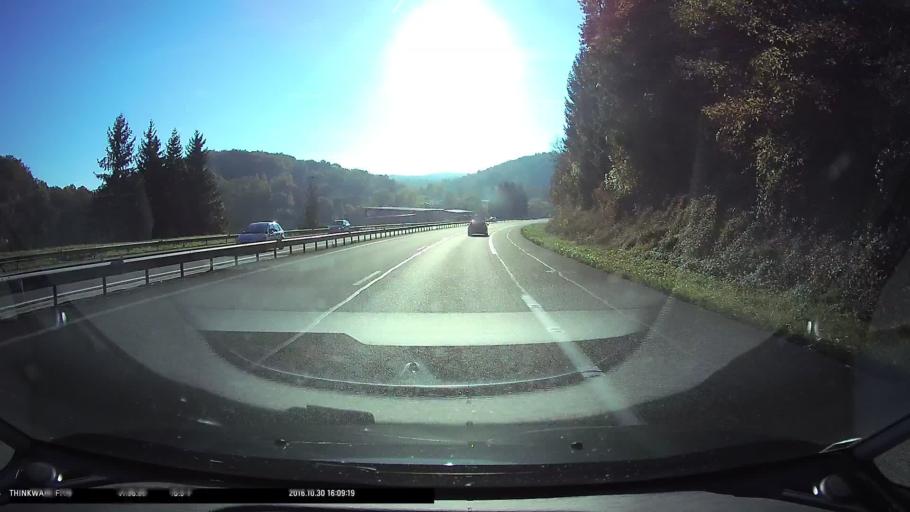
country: FR
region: Franche-Comte
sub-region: Departement du Doubs
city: Colombier-Fontaine
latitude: 47.4248
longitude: 6.6883
